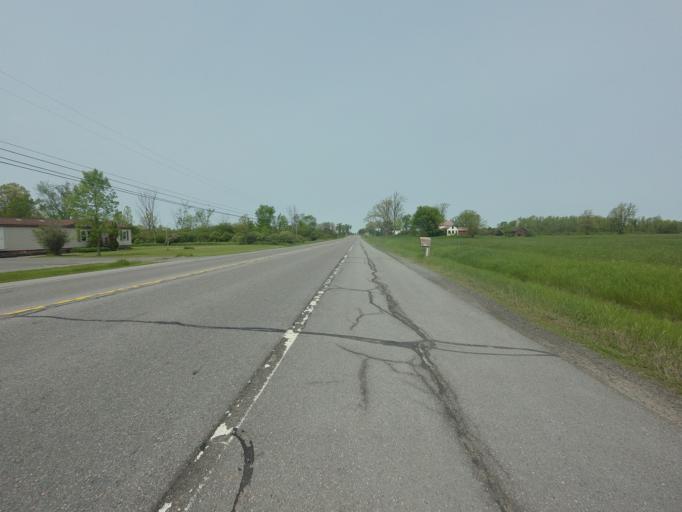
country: US
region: New York
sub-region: Jefferson County
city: Dexter
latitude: 44.0345
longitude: -76.0613
